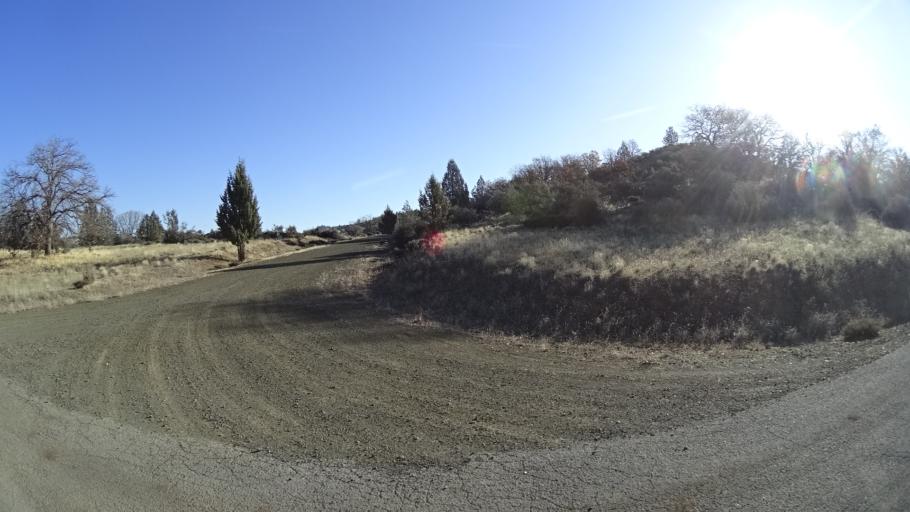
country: US
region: California
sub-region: Siskiyou County
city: Montague
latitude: 41.8904
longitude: -122.4891
